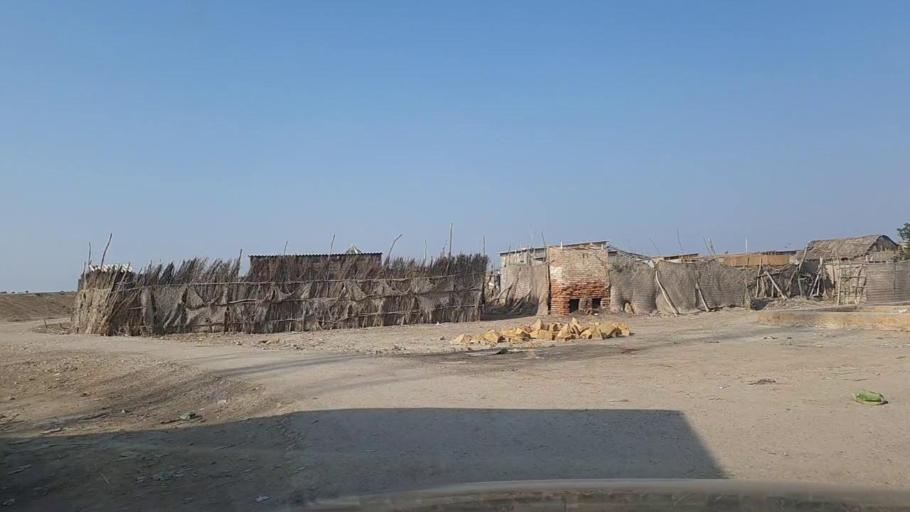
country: PK
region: Sindh
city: Keti Bandar
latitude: 24.1442
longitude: 67.4499
